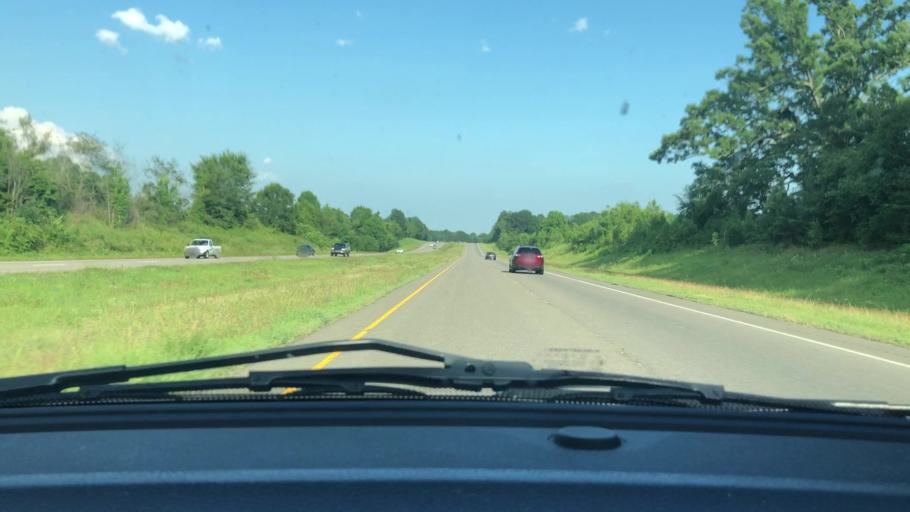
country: US
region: North Carolina
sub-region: Chatham County
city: Farmville
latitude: 35.6076
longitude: -79.3335
